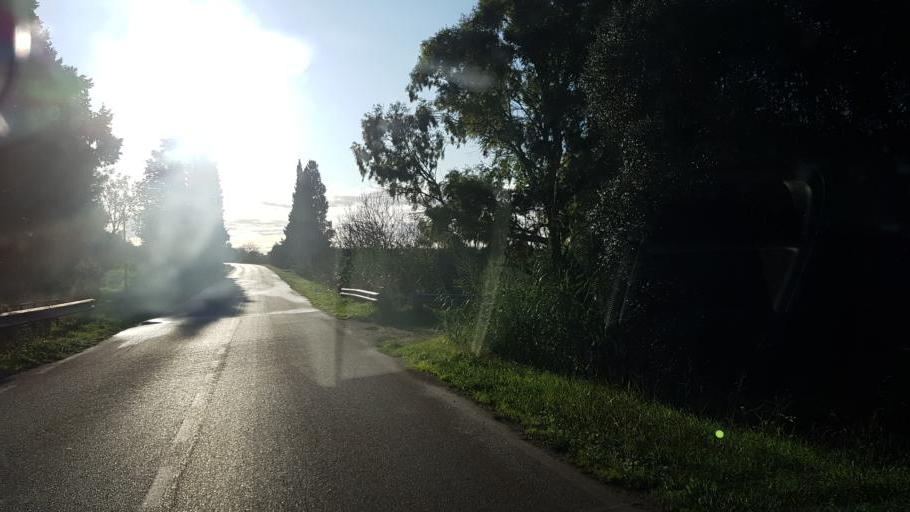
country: IT
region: Apulia
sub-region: Provincia di Brindisi
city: Torchiarolo
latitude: 40.5469
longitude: 18.0434
